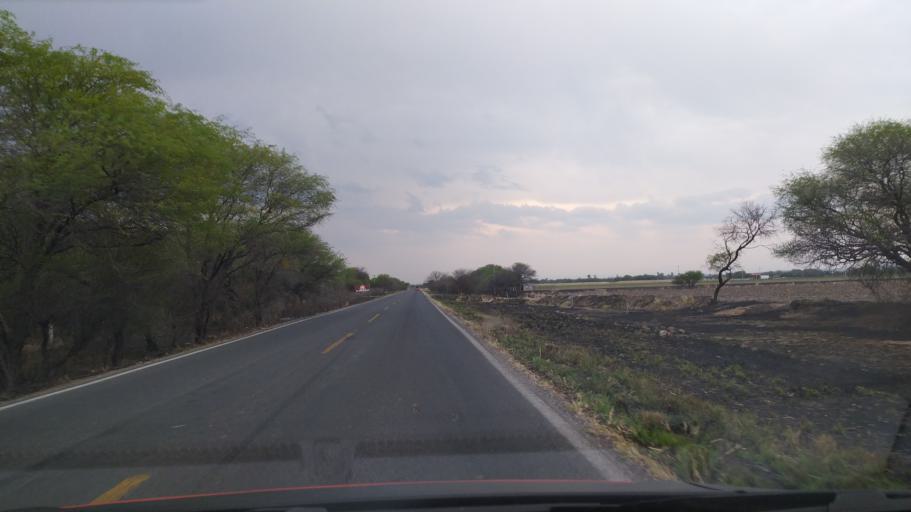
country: MX
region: Guanajuato
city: Ciudad Manuel Doblado
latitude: 20.7692
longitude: -101.9135
